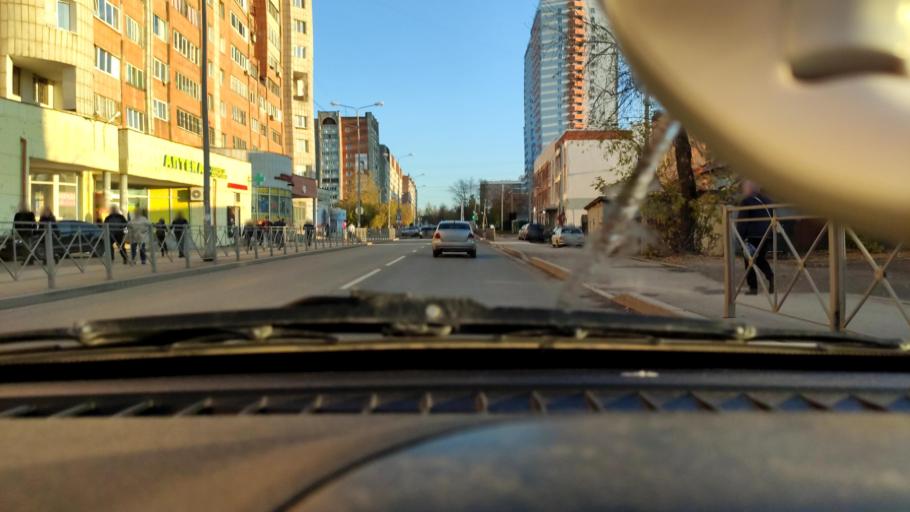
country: RU
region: Perm
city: Perm
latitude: 57.9788
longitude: 56.2027
